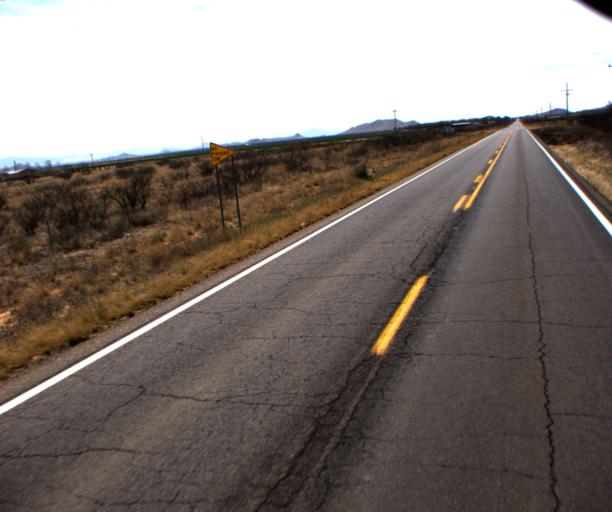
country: US
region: Arizona
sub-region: Cochise County
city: Willcox
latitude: 31.9795
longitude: -109.8507
